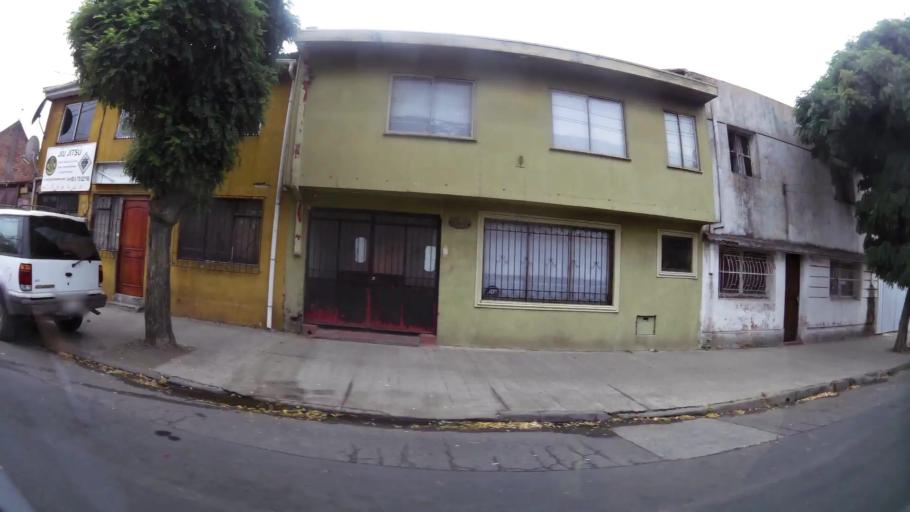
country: CL
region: Biobio
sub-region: Provincia de Concepcion
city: Concepcion
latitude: -36.8225
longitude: -73.0592
